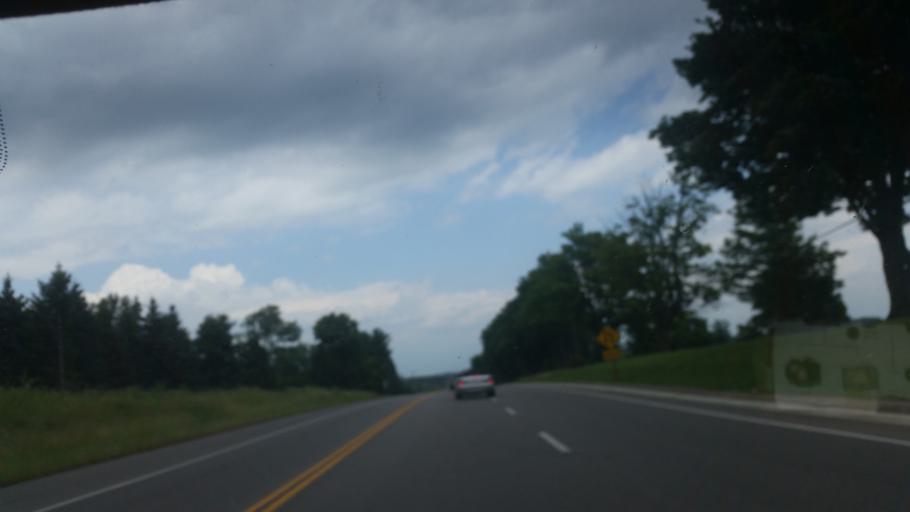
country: CA
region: Ontario
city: Orangeville
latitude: 43.7122
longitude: -80.1186
